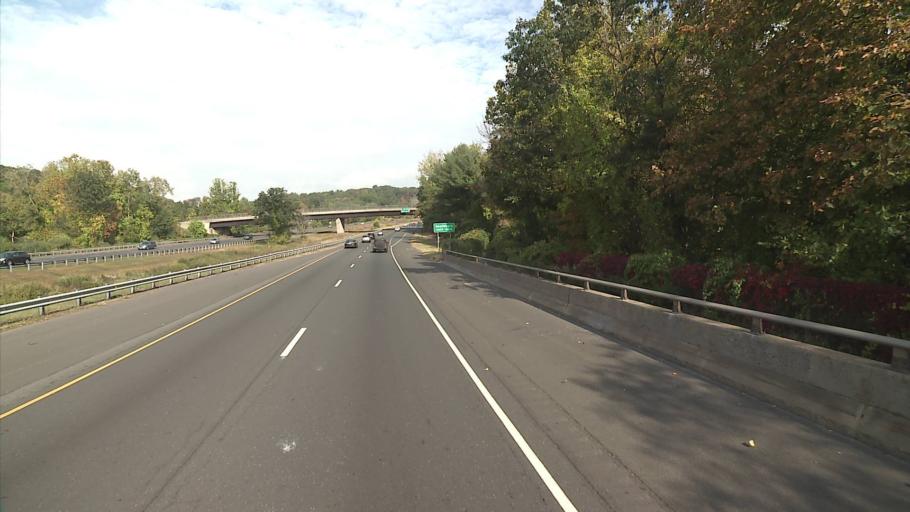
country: US
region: Connecticut
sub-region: New Haven County
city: Heritage Village
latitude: 41.4405
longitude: -73.2482
